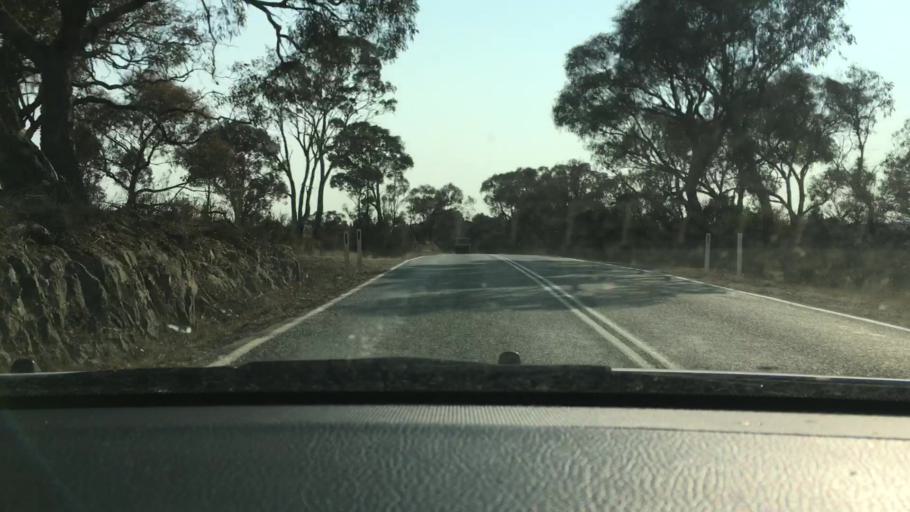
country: AU
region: New South Wales
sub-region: Queanbeyan
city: Queanbeyan
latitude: -35.4082
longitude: 149.2268
